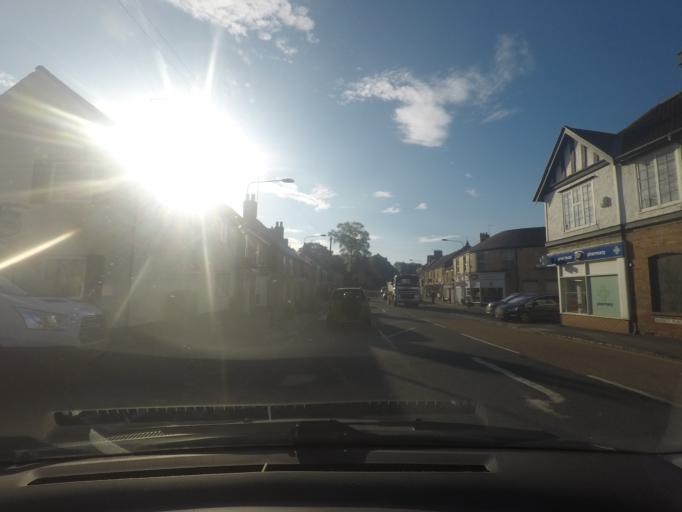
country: GB
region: England
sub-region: East Riding of Yorkshire
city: South Cave
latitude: 53.7695
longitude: -0.6005
